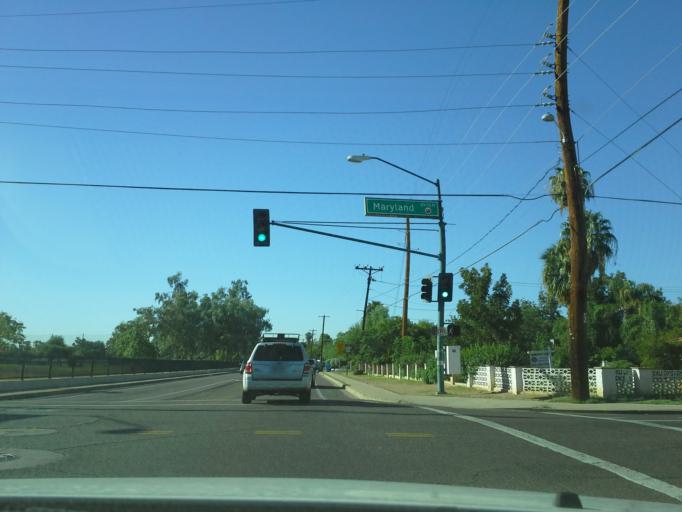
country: US
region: Arizona
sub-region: Maricopa County
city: Phoenix
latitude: 33.5314
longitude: -112.0912
